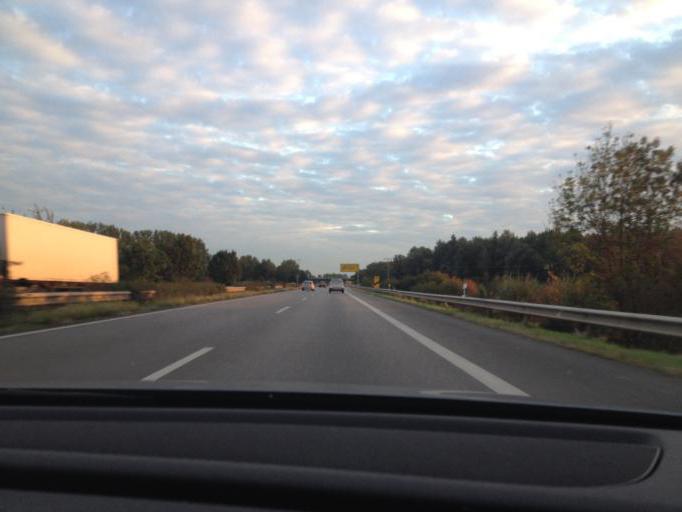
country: DE
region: Rheinland-Pfalz
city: Neuhofen
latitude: 49.4281
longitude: 8.4086
